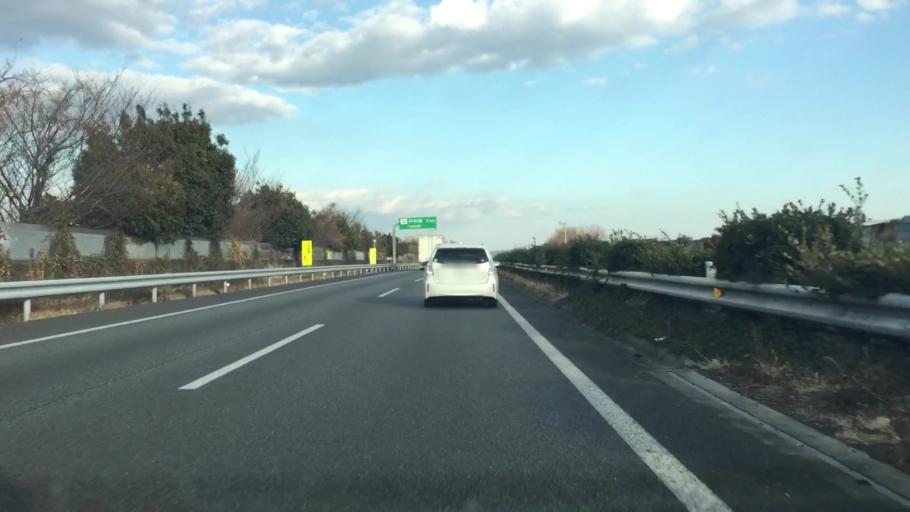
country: JP
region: Gunma
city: Isesaki
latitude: 36.3551
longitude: 139.1942
